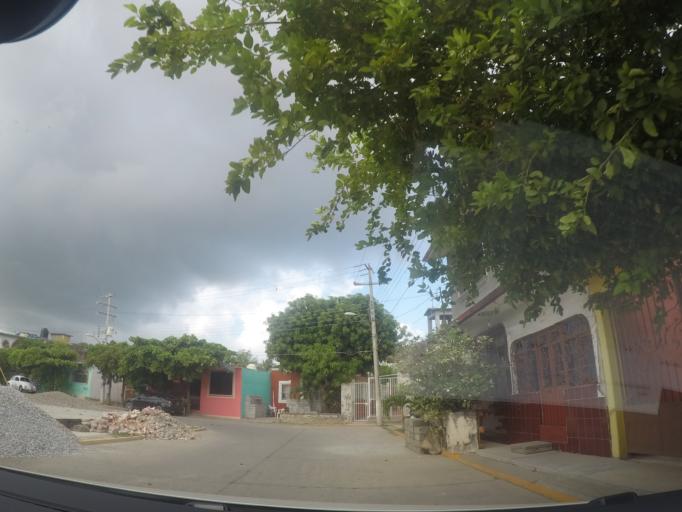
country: MX
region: Oaxaca
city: Juchitan de Zaragoza
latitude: 16.4343
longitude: -95.0338
